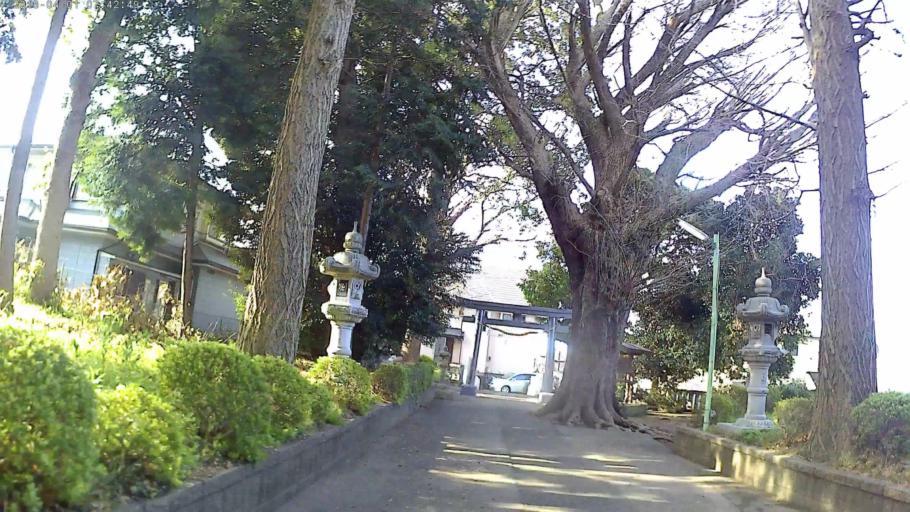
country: JP
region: Kanagawa
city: Atsugi
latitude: 35.4371
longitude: 139.4084
